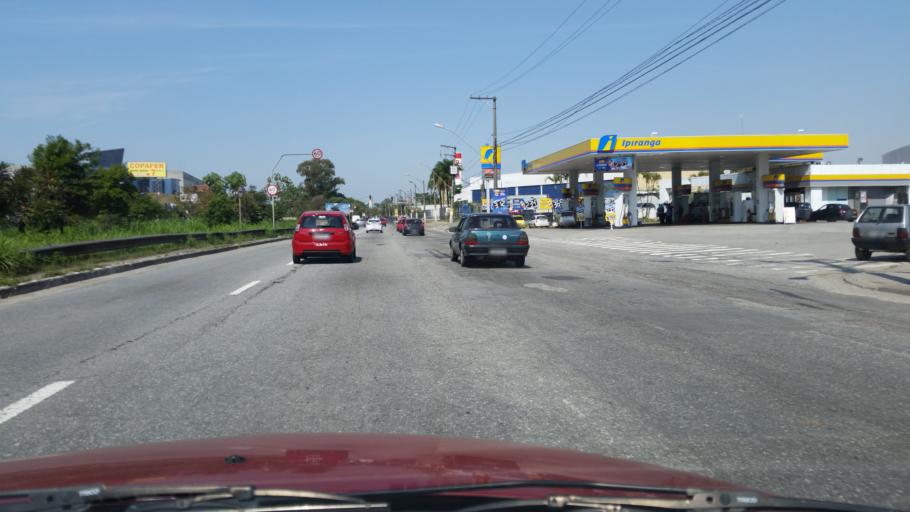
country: BR
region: Sao Paulo
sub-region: Santo Andre
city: Santo Andre
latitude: -23.6527
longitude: -46.5107
